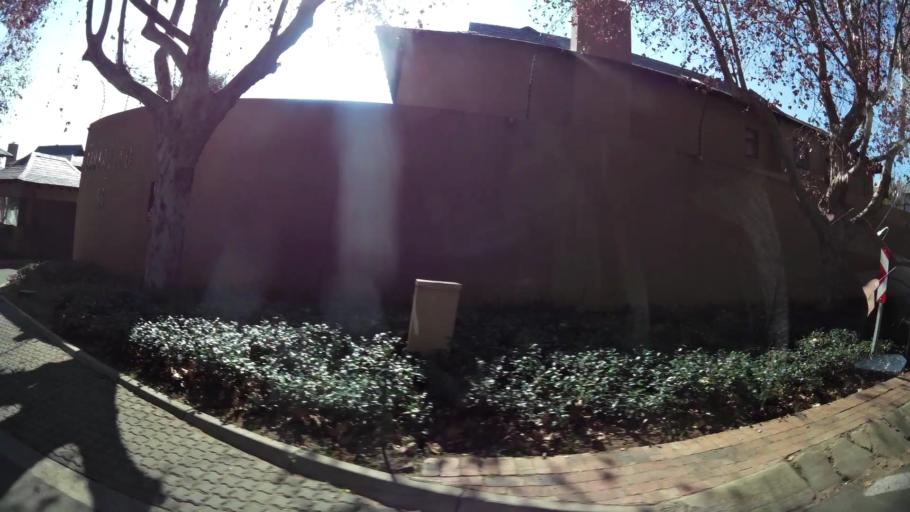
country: ZA
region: Gauteng
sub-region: City of Johannesburg Metropolitan Municipality
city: Johannesburg
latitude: -26.1088
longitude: 28.0356
